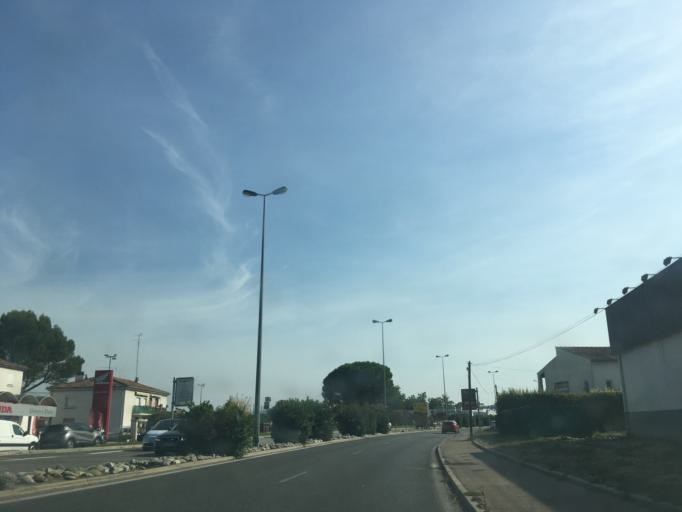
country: FR
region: Provence-Alpes-Cote d'Azur
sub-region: Departement du Var
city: Trans-en-Provence
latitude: 43.5082
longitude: 6.4817
